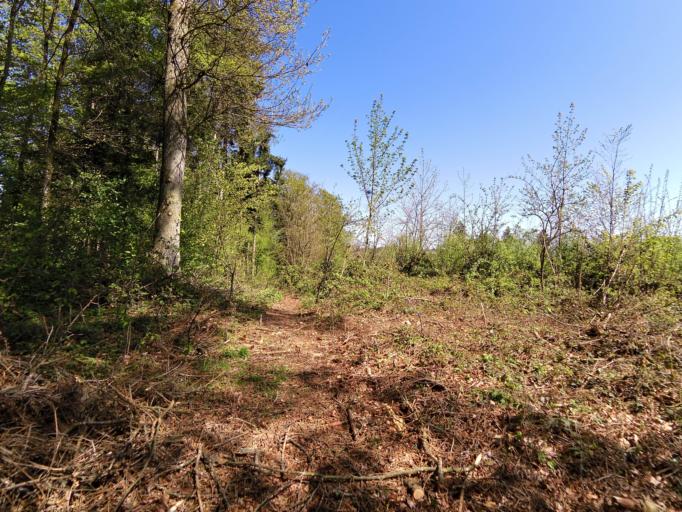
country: CH
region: Thurgau
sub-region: Weinfelden District
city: Berg
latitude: 47.6052
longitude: 9.1328
